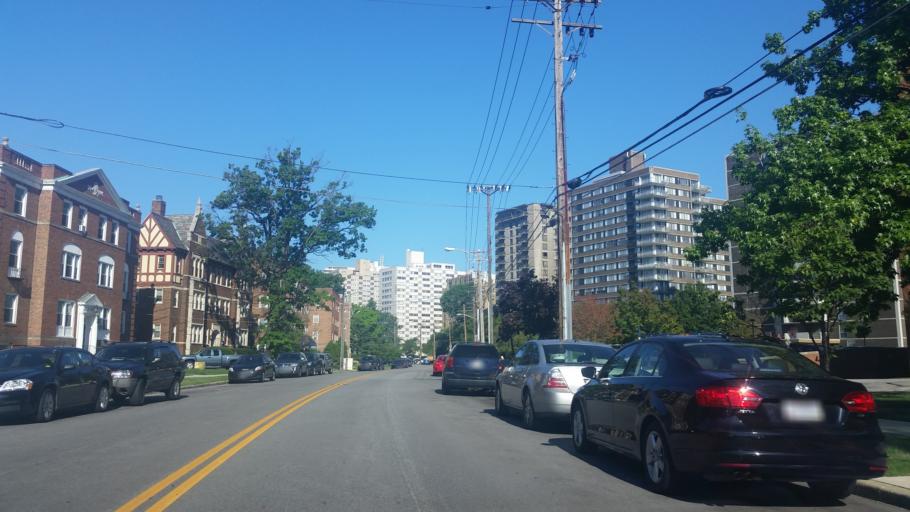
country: US
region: Ohio
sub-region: Cuyahoga County
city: Lakewood
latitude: 41.4908
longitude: -81.7719
